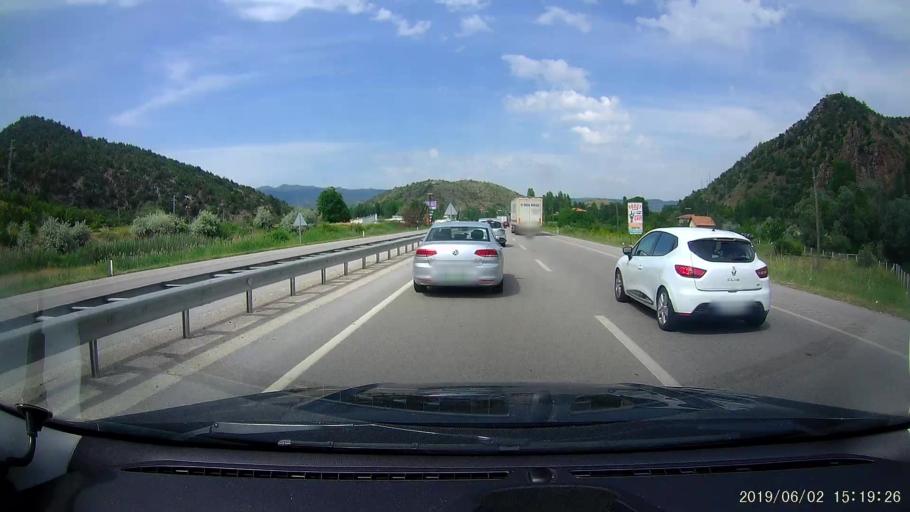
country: TR
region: Corum
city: Osmancik
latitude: 40.9708
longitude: 34.9092
